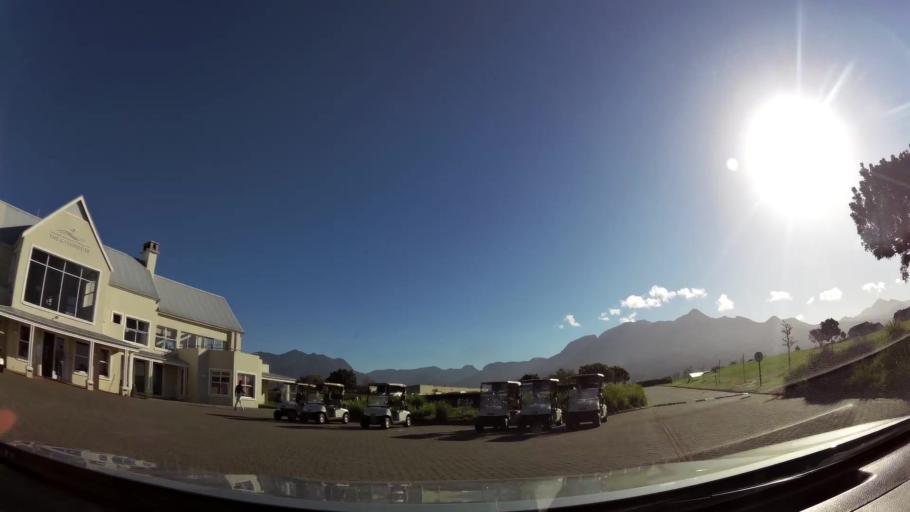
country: ZA
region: Western Cape
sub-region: Eden District Municipality
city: George
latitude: -33.9689
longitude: 22.4299
